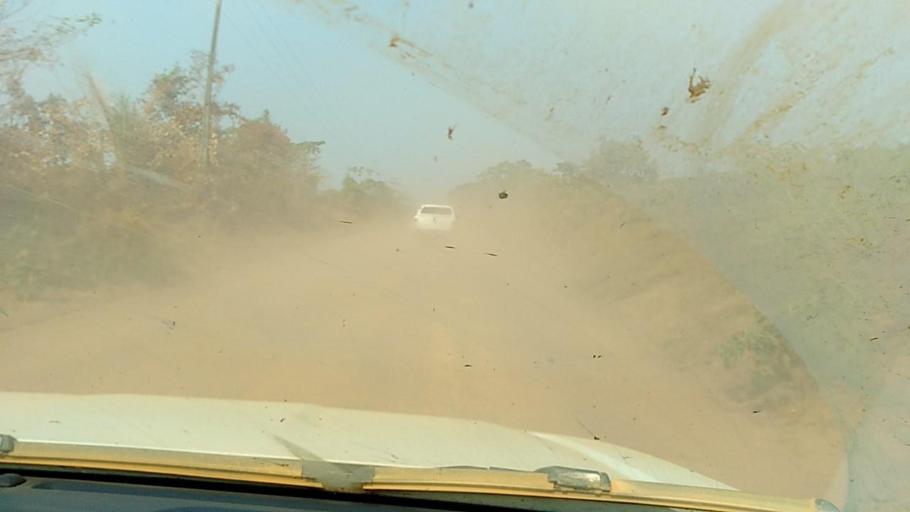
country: BR
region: Rondonia
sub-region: Porto Velho
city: Porto Velho
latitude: -8.8401
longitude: -64.1525
